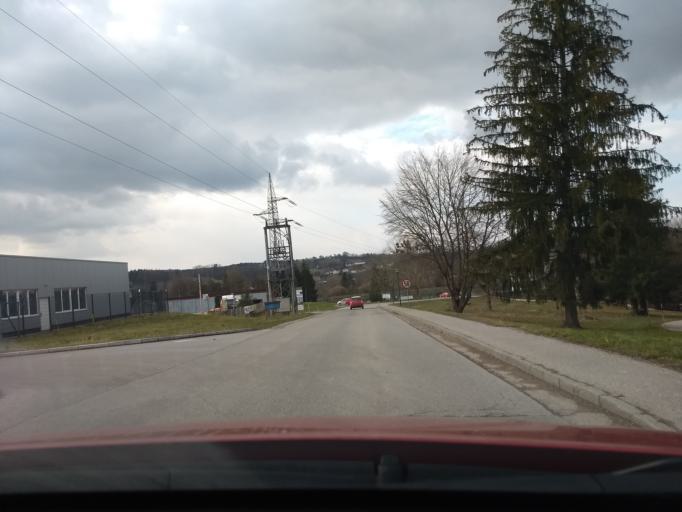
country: AT
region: Upper Austria
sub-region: Politischer Bezirk Steyr-Land
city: Garsten
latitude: 48.0164
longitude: 14.4132
